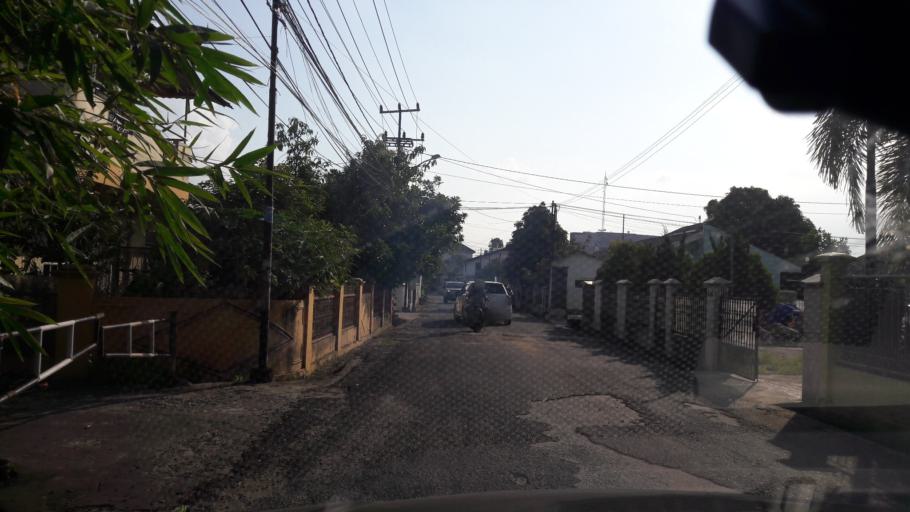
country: ID
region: South Sumatra
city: Plaju
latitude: -3.0025
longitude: 104.7241
